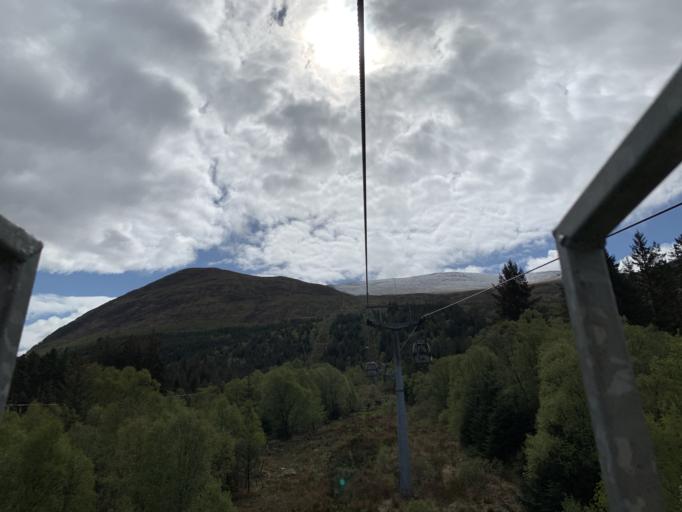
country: GB
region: Scotland
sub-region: Highland
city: Spean Bridge
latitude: 56.8480
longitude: -4.9918
